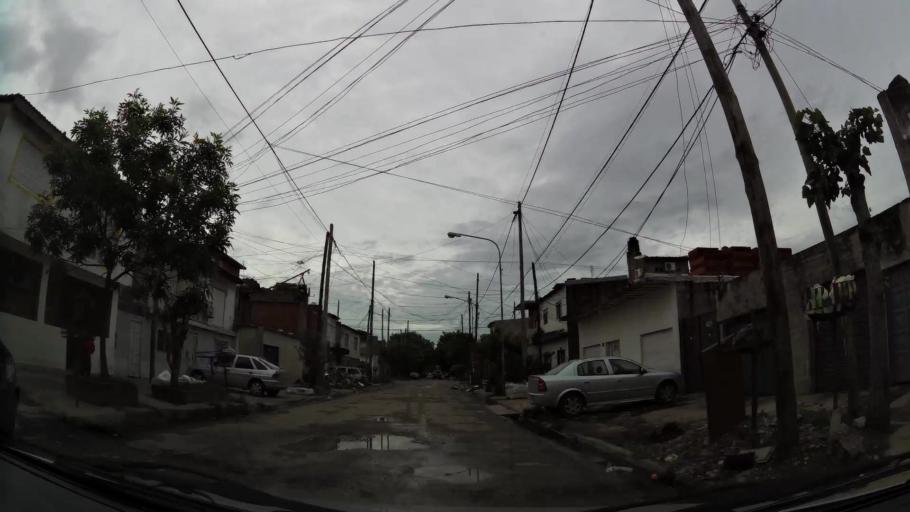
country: AR
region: Buenos Aires
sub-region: Partido de Lanus
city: Lanus
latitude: -34.7238
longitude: -58.3749
